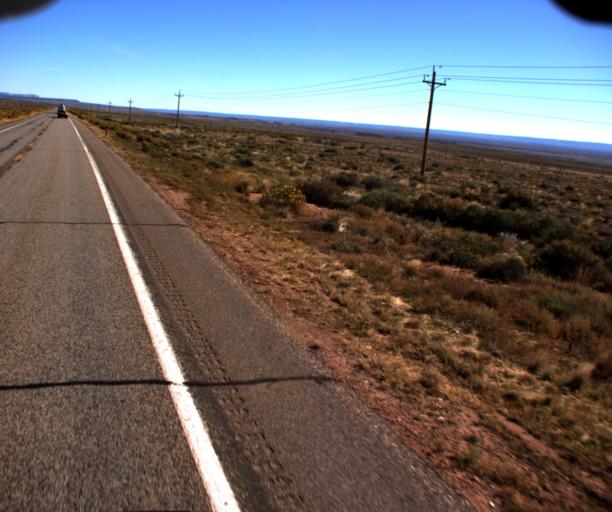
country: US
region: Arizona
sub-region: Coconino County
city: Fredonia
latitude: 36.8815
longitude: -112.6406
